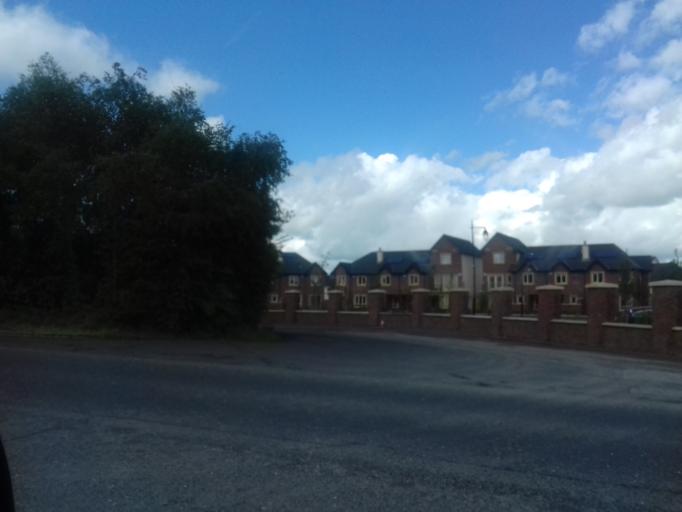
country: IE
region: Leinster
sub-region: Kildare
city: Maynooth
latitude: 53.3694
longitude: -6.5909
